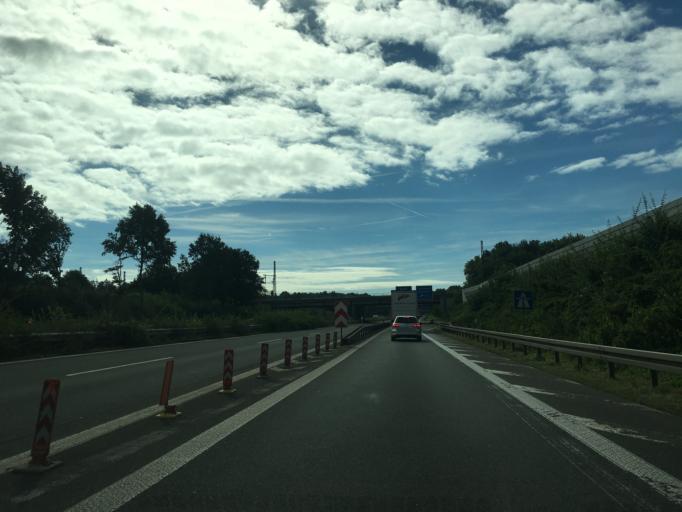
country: DE
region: North Rhine-Westphalia
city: Bad Oeynhausen
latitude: 52.2101
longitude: 8.8369
